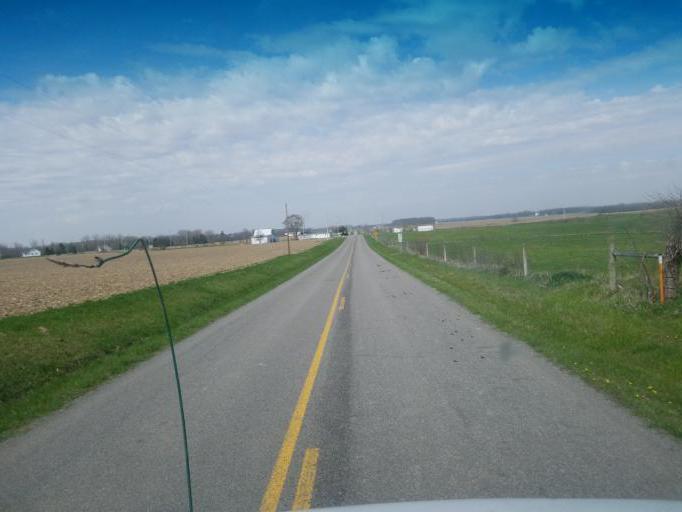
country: US
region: Ohio
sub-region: Logan County
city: Northwood
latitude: 40.4940
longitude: -83.7026
